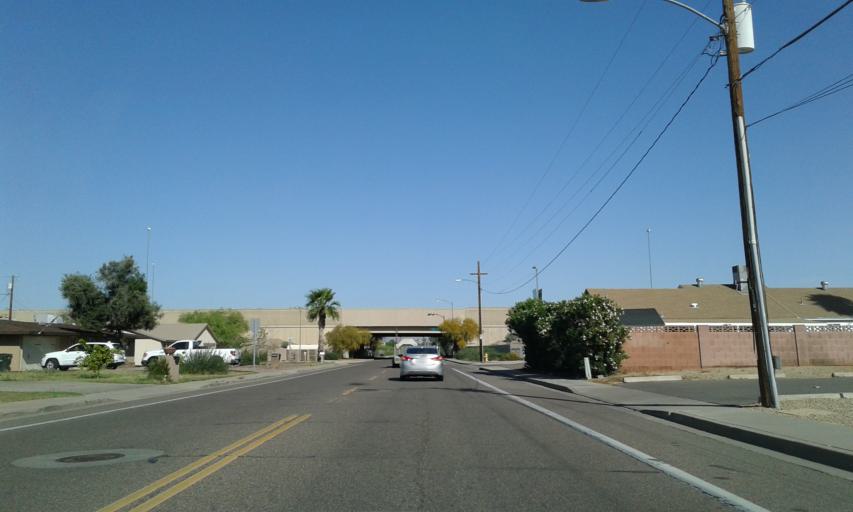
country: US
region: Arizona
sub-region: Maricopa County
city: Paradise Valley
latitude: 33.6043
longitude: -112.0115
